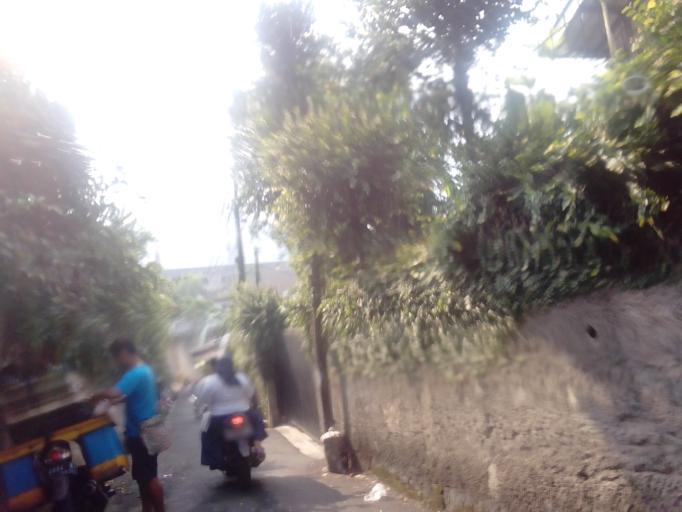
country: ID
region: Jakarta Raya
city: Jakarta
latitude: -6.2596
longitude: 106.8071
